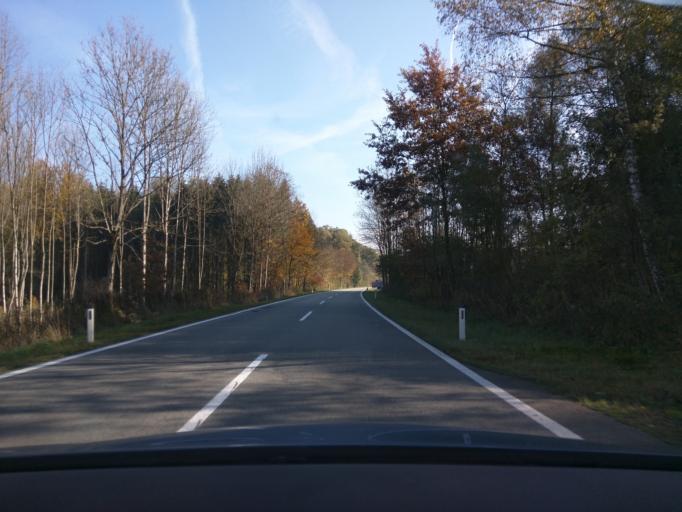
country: DE
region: Bavaria
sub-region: Lower Bavaria
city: Thyrnau
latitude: 48.5842
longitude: 13.5231
